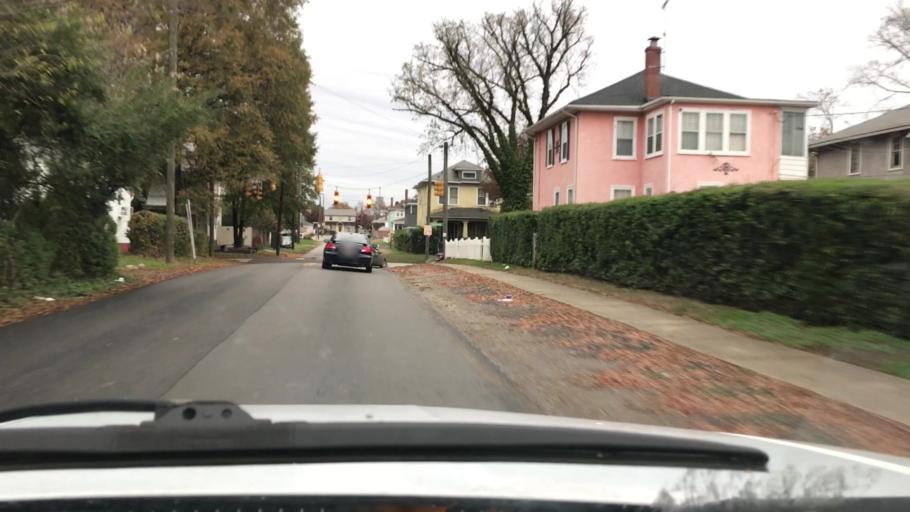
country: US
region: Virginia
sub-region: City of Richmond
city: Richmond
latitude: 37.5651
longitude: -77.4421
